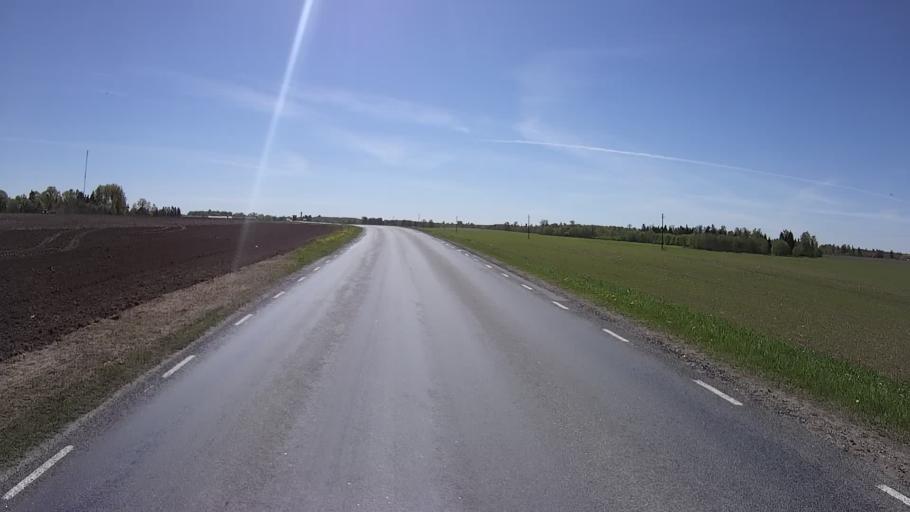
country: EE
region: Harju
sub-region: Raasiku vald
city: Raasiku
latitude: 59.1164
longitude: 25.1689
